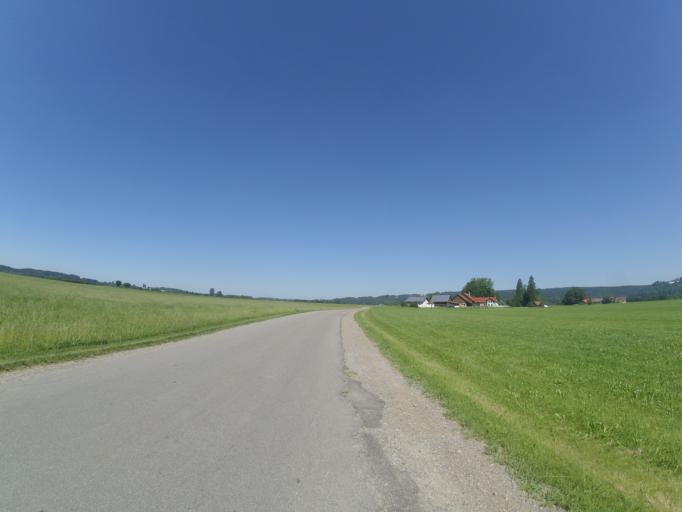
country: DE
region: Baden-Wuerttemberg
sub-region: Tuebingen Region
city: Leutkirch im Allgau
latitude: 47.8432
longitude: 10.0027
